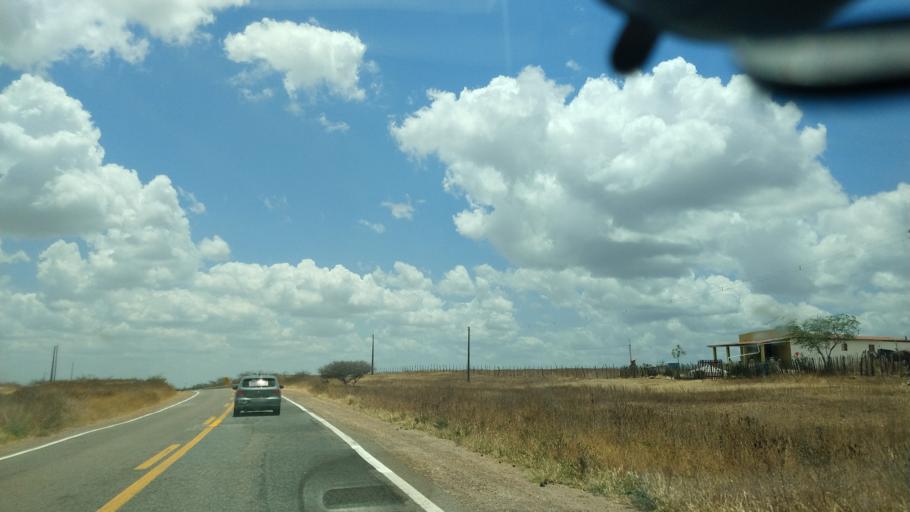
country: BR
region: Rio Grande do Norte
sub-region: Cerro Cora
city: Cerro Cora
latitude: -6.1900
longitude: -36.2541
